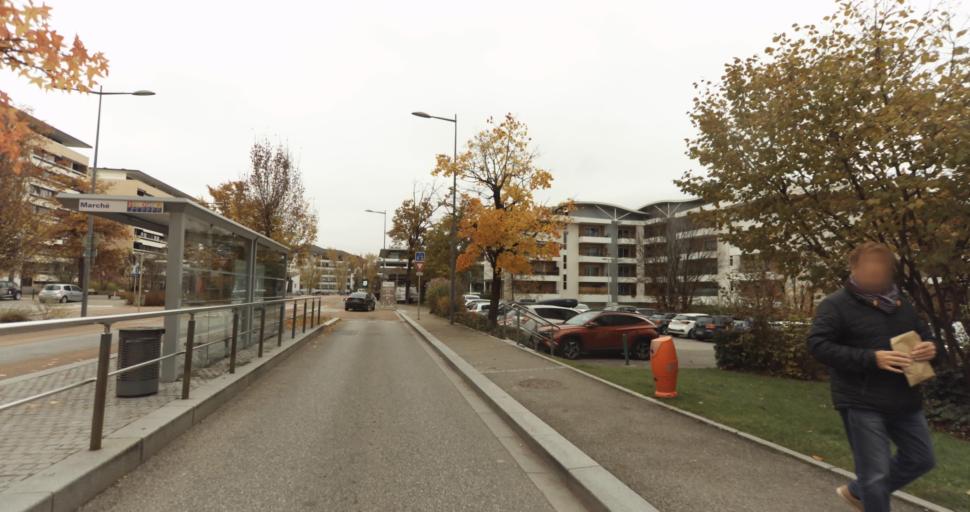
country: FR
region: Rhone-Alpes
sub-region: Departement de la Haute-Savoie
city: Cran-Gevrier
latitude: 45.8884
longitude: 6.1002
